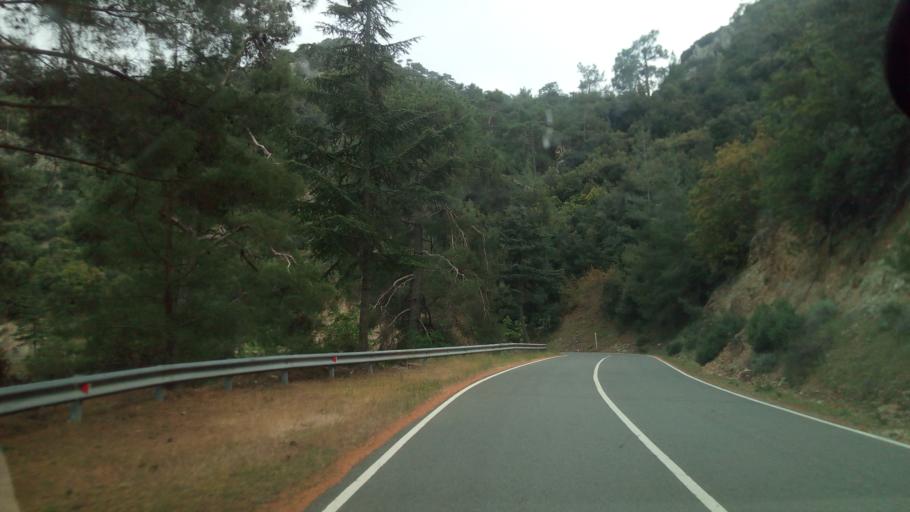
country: CY
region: Lefkosia
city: Kato Pyrgos
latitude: 35.0115
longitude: 32.6734
